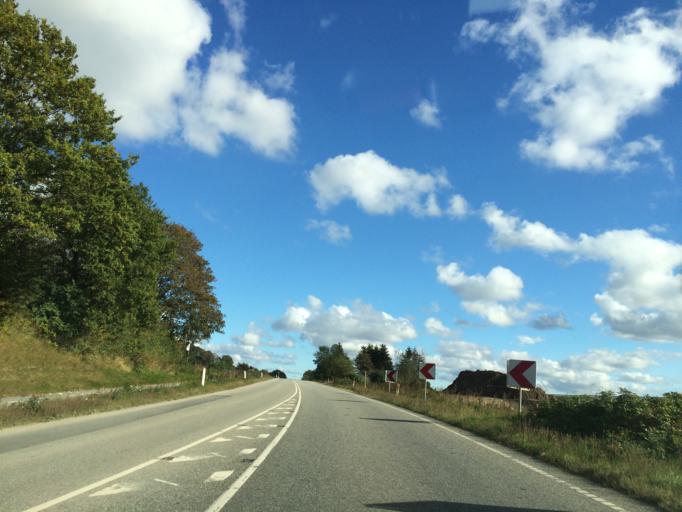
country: DK
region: Central Jutland
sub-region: Skanderborg Kommune
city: Ry
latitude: 56.1495
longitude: 9.7708
